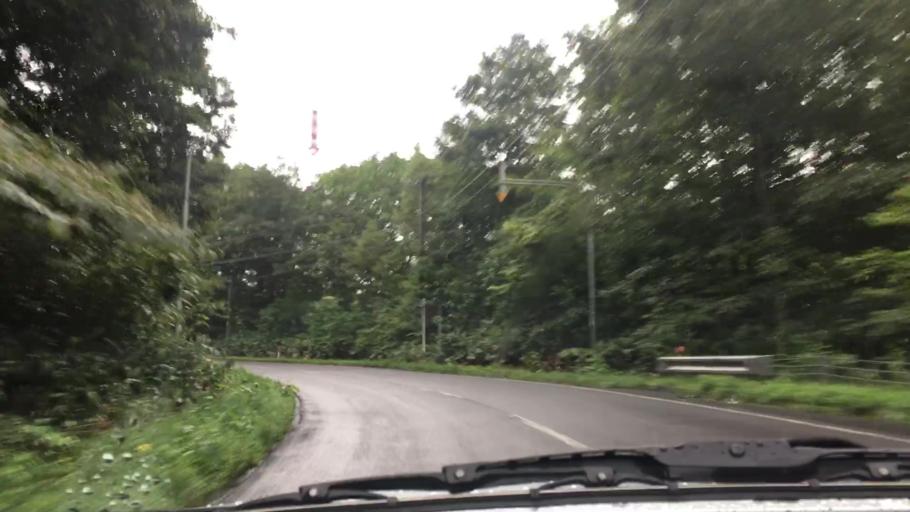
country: JP
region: Hokkaido
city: Niseko Town
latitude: 42.6289
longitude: 140.7198
